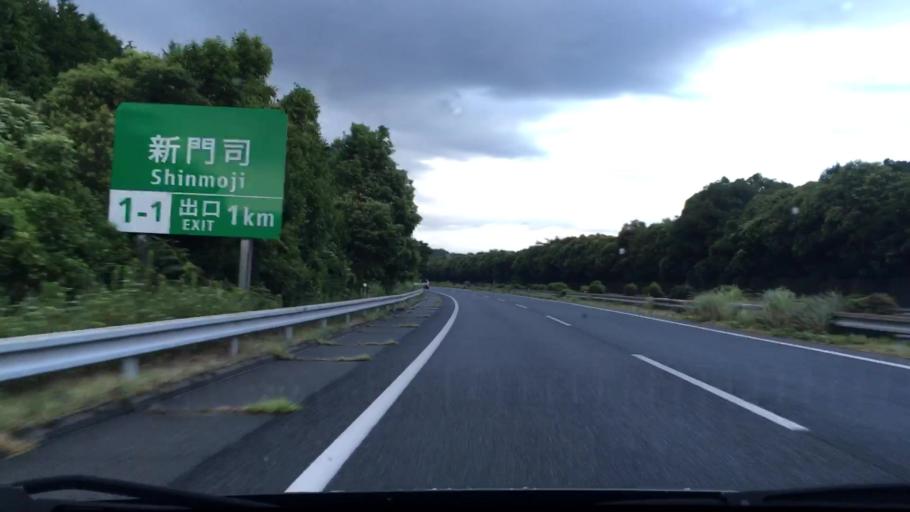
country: JP
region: Yamaguchi
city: Shimonoseki
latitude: 33.8765
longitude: 130.9689
